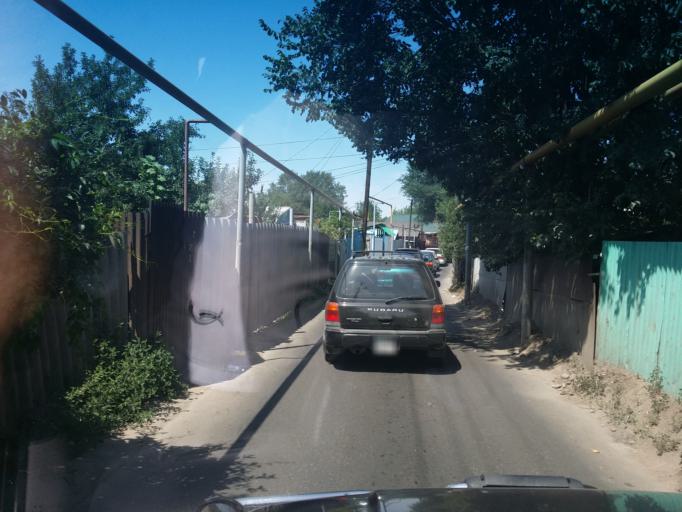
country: KZ
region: Almaty Qalasy
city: Almaty
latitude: 43.2646
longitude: 76.9127
